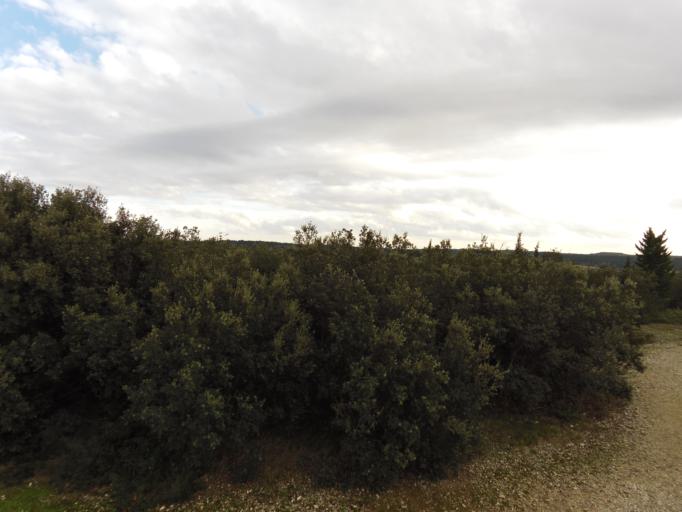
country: FR
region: Languedoc-Roussillon
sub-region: Departement du Gard
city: La Calmette
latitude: 43.8876
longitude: 4.2638
